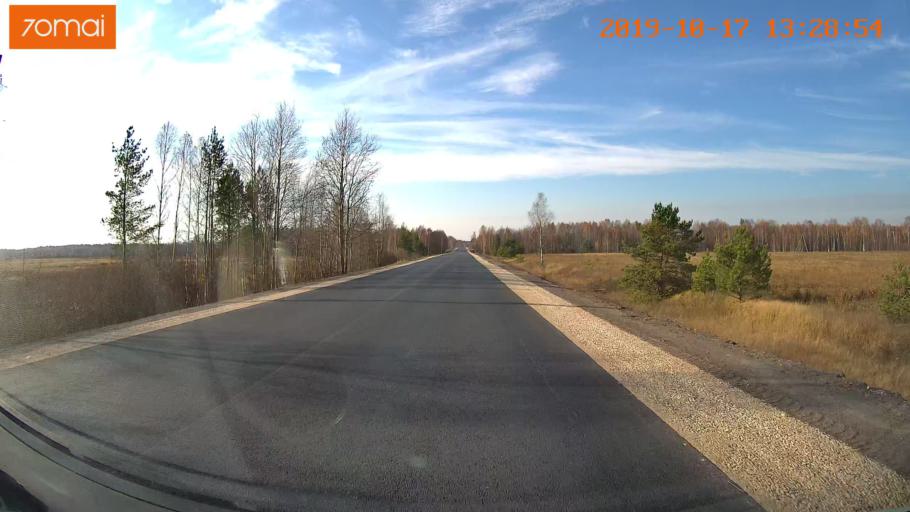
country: RU
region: Vladimir
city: Velikodvorskiy
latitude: 55.1177
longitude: 40.8559
